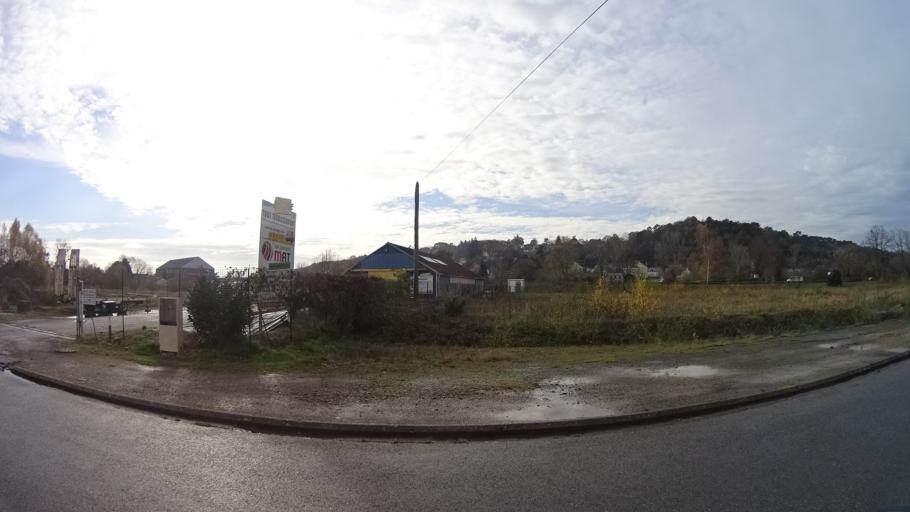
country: FR
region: Brittany
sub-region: Departement d'Ille-et-Vilaine
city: Redon
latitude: 47.6352
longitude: -2.1003
